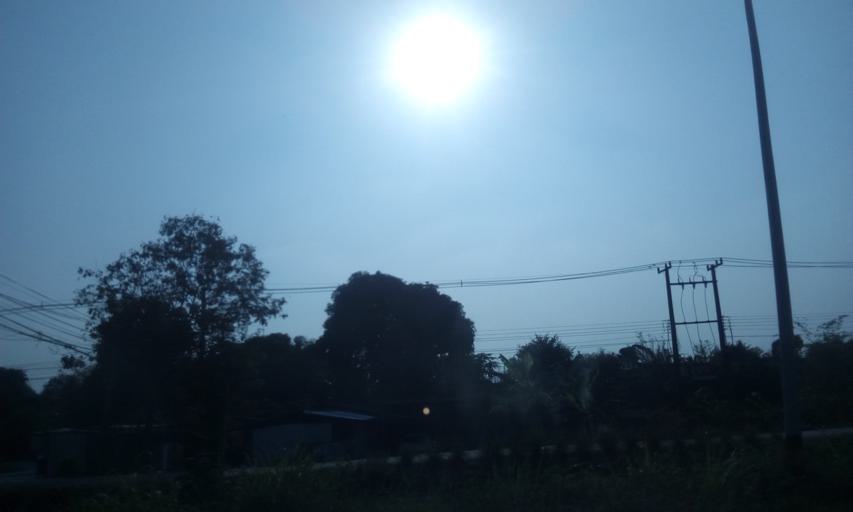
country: TH
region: Sing Buri
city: Sing Buri
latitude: 14.8525
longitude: 100.4133
